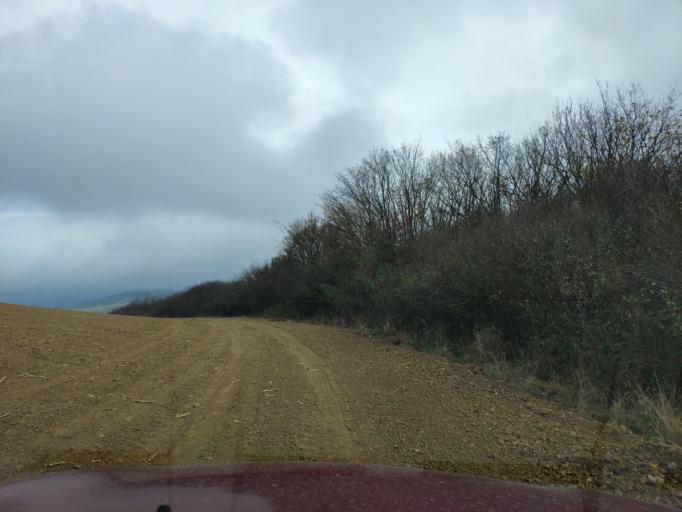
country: SK
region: Presovsky
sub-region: Okres Presov
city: Presov
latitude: 49.0043
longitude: 21.2021
